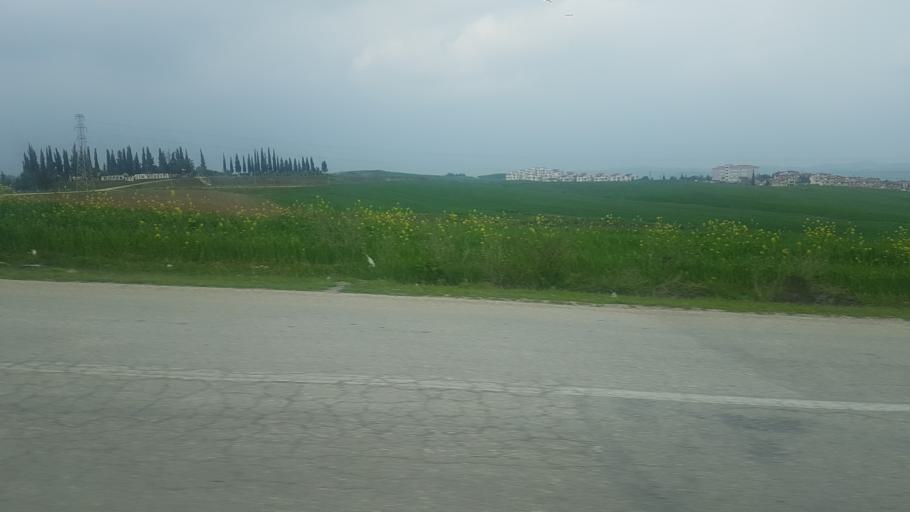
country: TR
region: Adana
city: Seyhan
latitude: 37.0587
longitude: 35.2323
